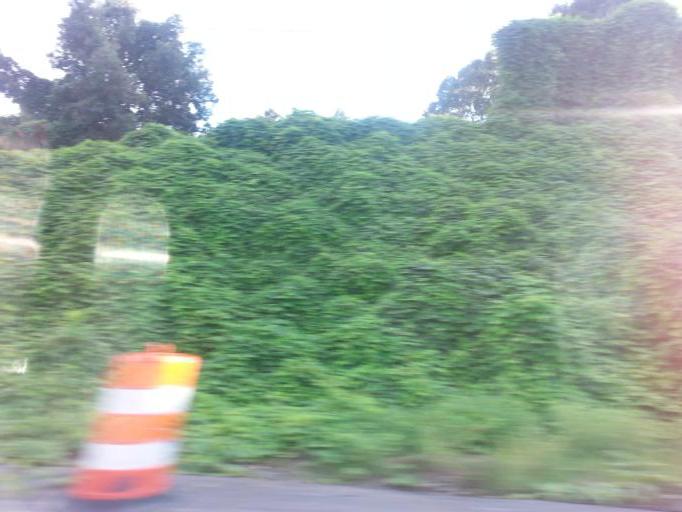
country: US
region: Alabama
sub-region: Lauderdale County
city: Killen
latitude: 34.8589
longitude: -87.4183
